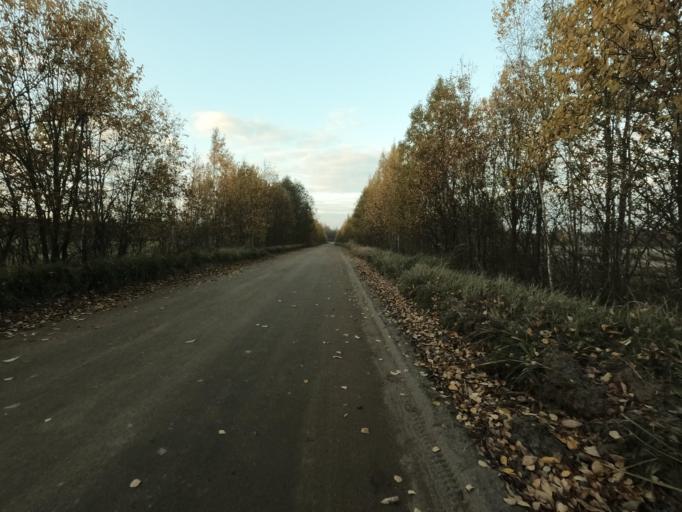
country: RU
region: Leningrad
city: Mga
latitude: 59.8034
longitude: 31.2007
